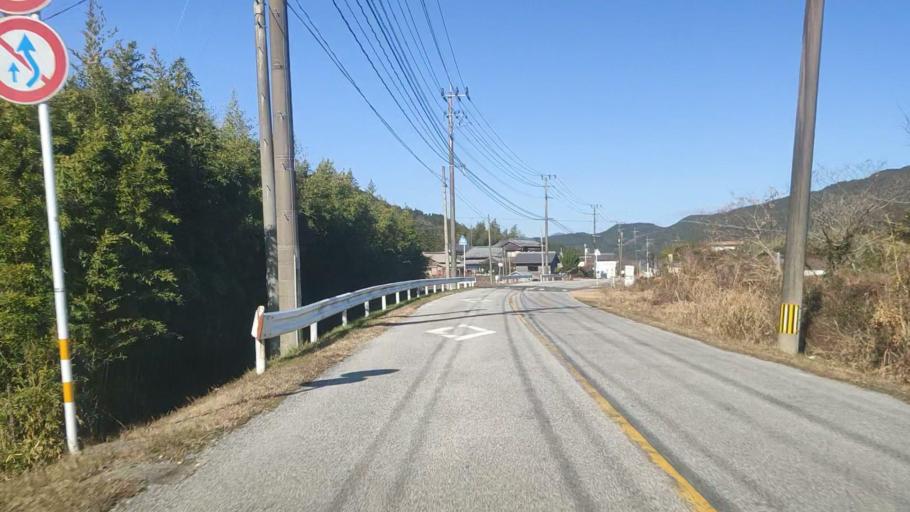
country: JP
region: Oita
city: Saiki
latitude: 32.9136
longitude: 131.9287
